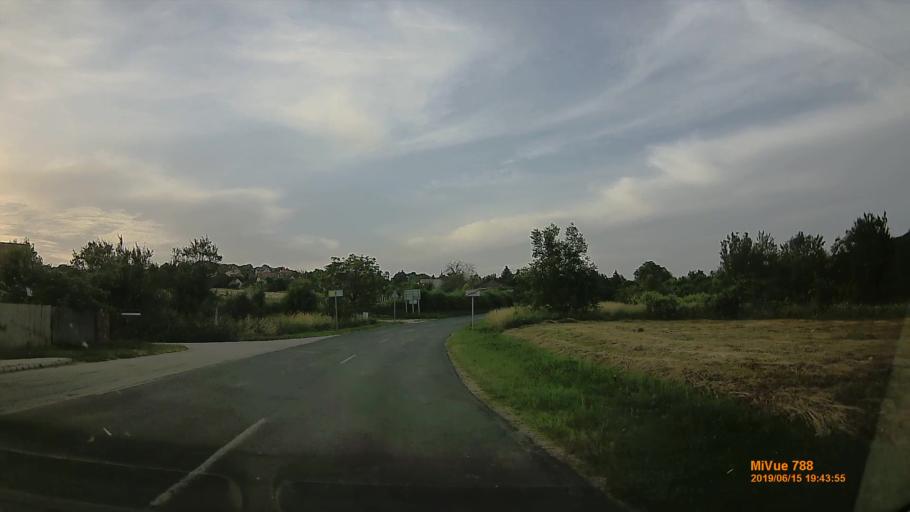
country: HU
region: Veszprem
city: Csopak
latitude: 46.9952
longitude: 17.9625
